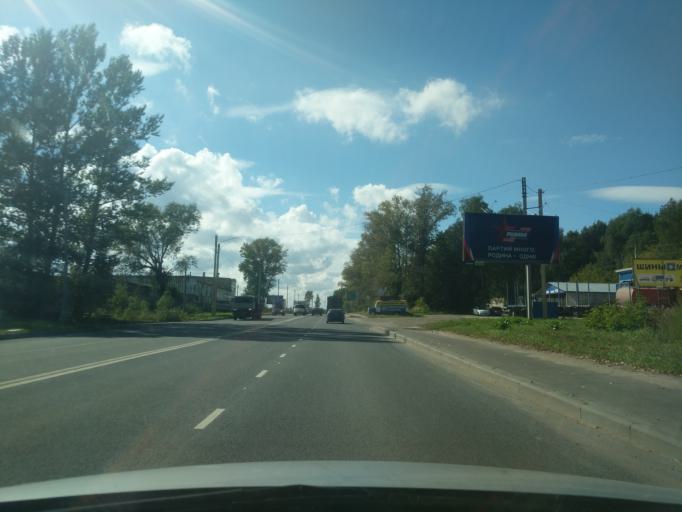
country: RU
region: Kostroma
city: Oktyabr'skiy
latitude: 57.7802
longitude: 40.9783
